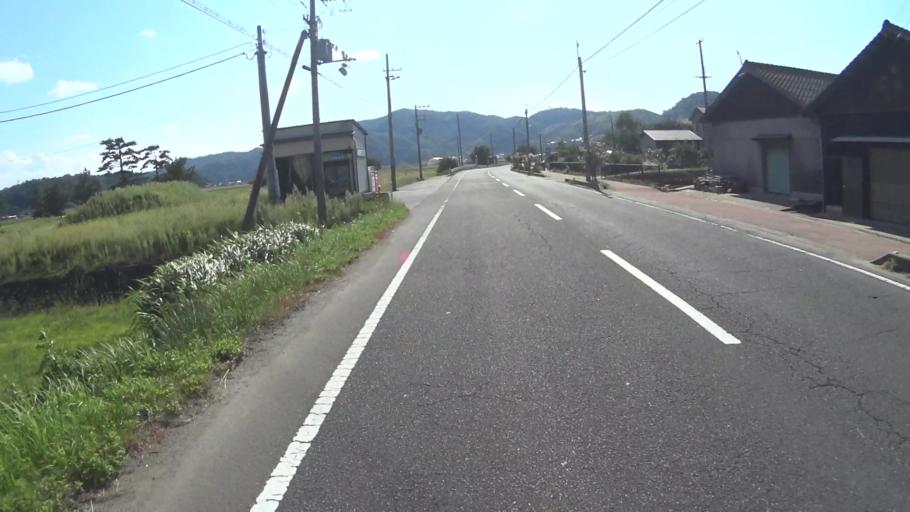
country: JP
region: Kyoto
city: Miyazu
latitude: 35.7393
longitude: 135.1085
